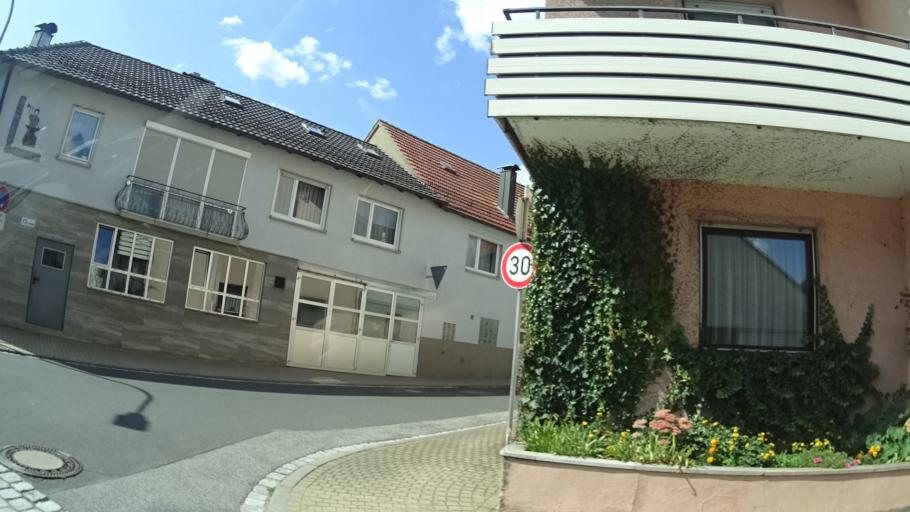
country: DE
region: Bavaria
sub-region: Regierungsbezirk Unterfranken
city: Ebelsbach
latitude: 49.9892
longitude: 10.6820
